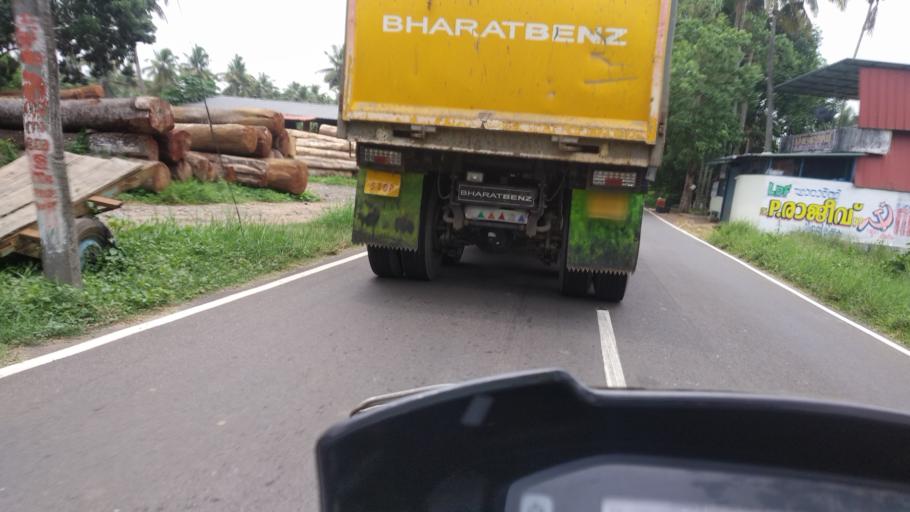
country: IN
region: Kerala
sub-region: Ernakulam
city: Aluva
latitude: 10.1562
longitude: 76.3086
